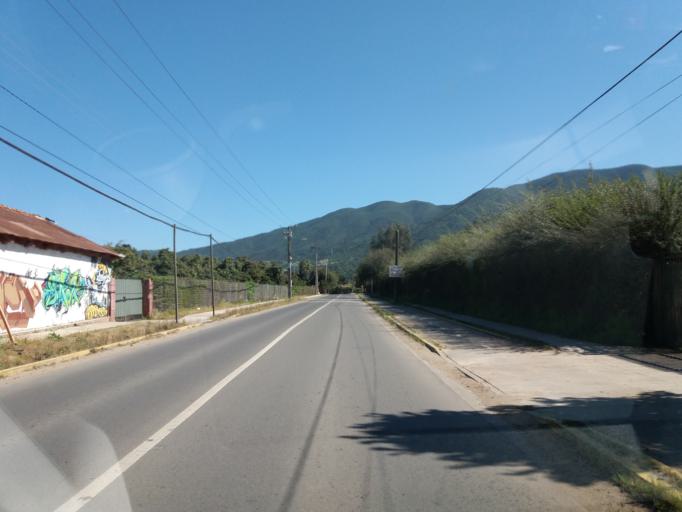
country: CL
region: Valparaiso
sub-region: Provincia de Marga Marga
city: Limache
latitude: -33.0009
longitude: -71.1774
